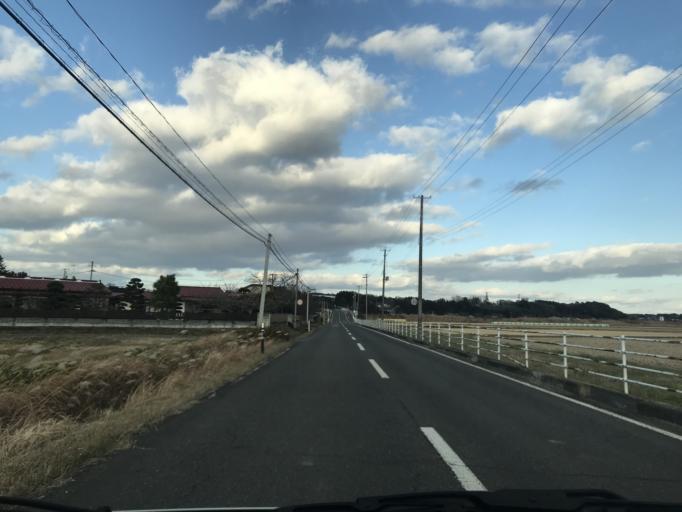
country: JP
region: Miyagi
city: Kogota
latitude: 38.6473
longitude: 141.0575
